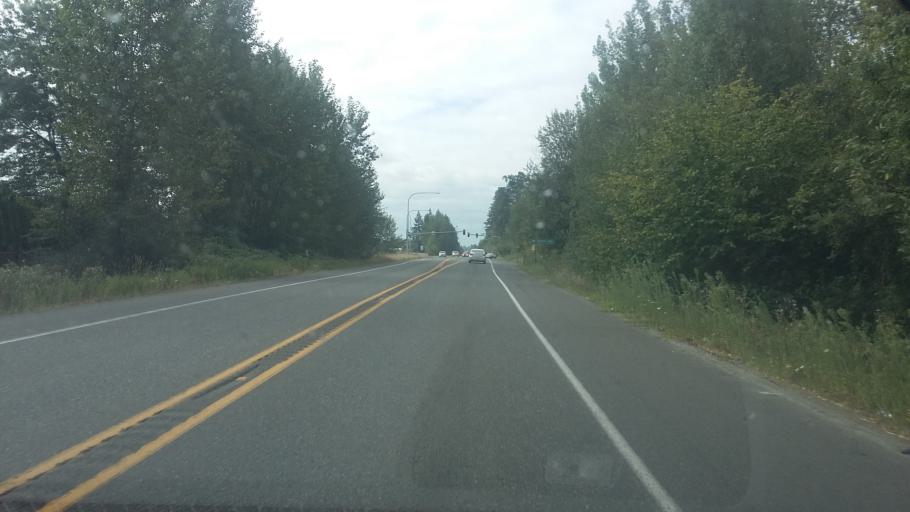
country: US
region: Washington
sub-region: Clark County
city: Battle Ground
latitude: 45.7938
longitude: -122.5475
